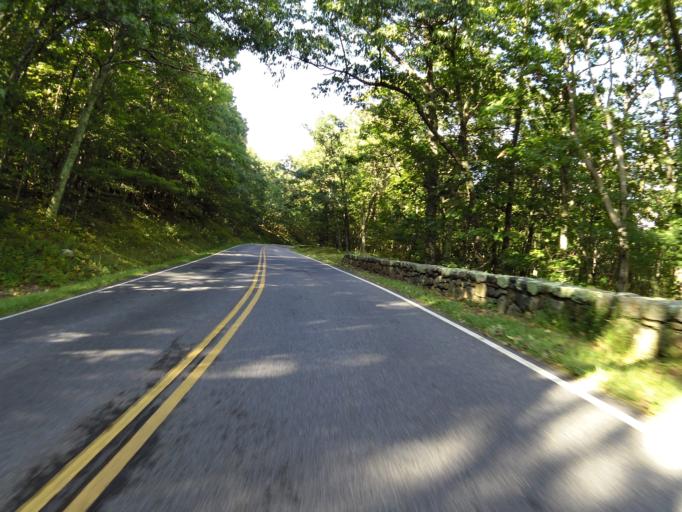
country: US
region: Virginia
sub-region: Page County
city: Stanley
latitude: 38.5408
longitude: -78.4141
